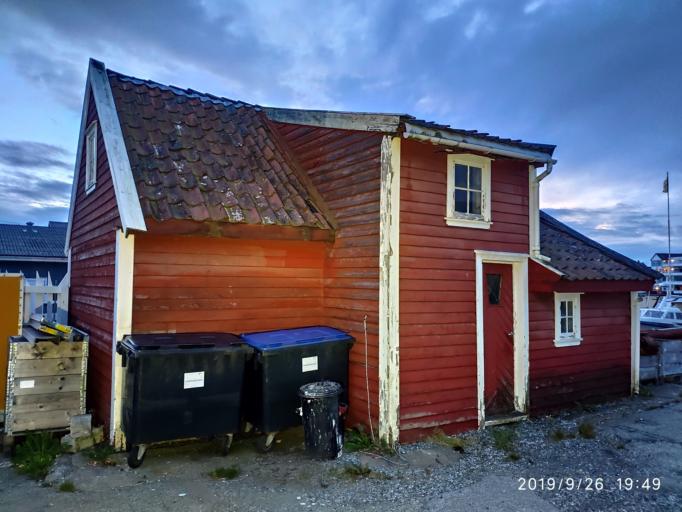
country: NO
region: Rogaland
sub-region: Haugesund
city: Haugesund
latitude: 59.4134
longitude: 5.2630
